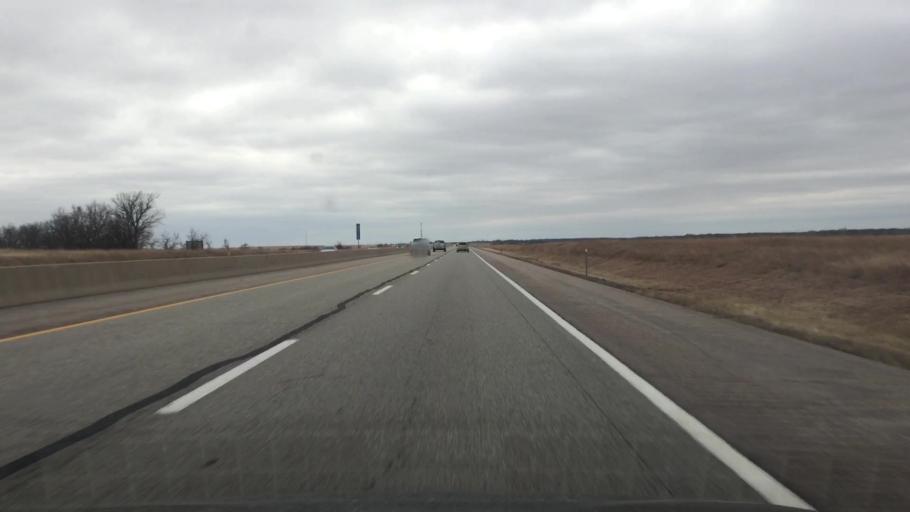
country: US
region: Kansas
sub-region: Butler County
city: El Dorado
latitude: 37.9805
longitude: -96.7119
